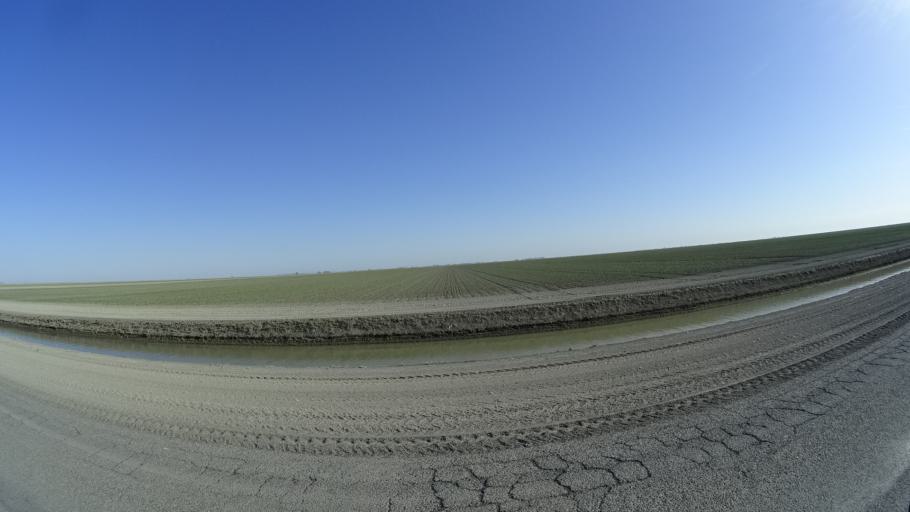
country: US
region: California
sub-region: Kings County
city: Stratford
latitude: 36.0796
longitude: -119.7869
